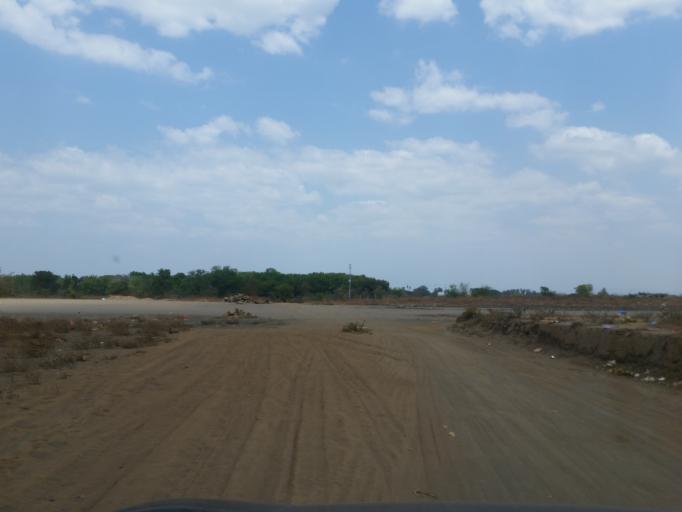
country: NI
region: Managua
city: Managua
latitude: 12.1341
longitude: -86.1613
